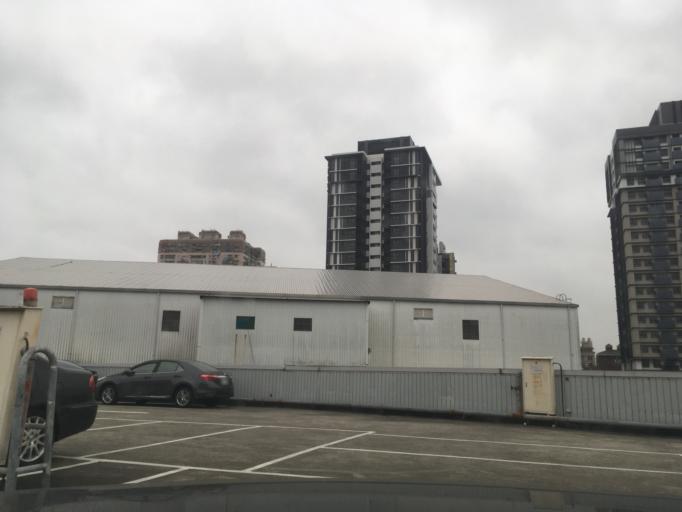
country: TW
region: Taipei
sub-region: Taipei
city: Banqiao
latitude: 24.9916
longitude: 121.4473
